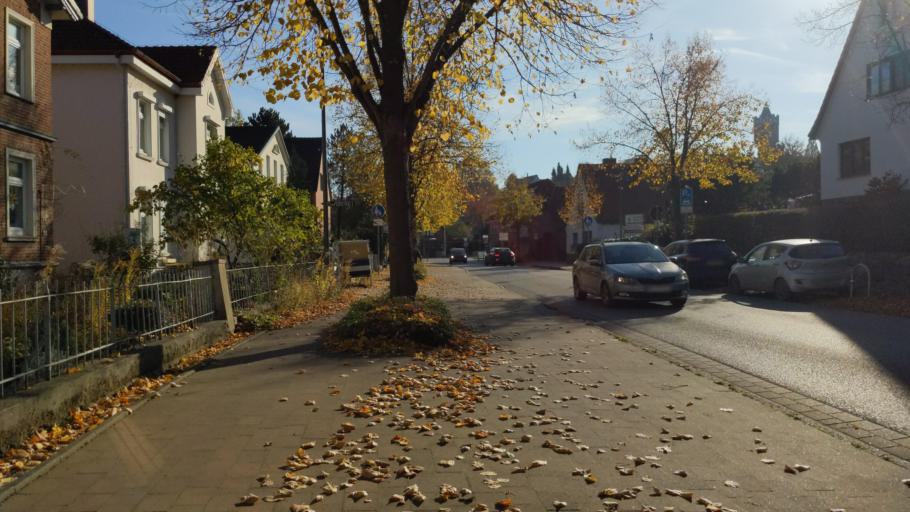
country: DE
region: Schleswig-Holstein
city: Eutin
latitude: 54.1430
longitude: 10.6124
